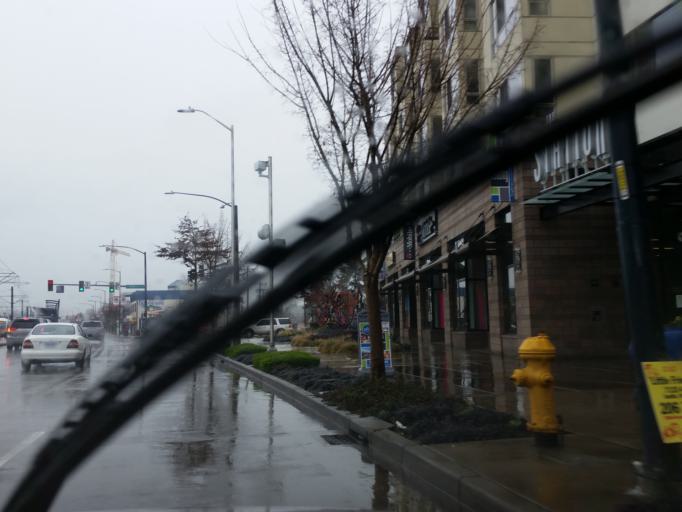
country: US
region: Washington
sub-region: King County
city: Riverton
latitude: 47.5364
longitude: -122.2807
